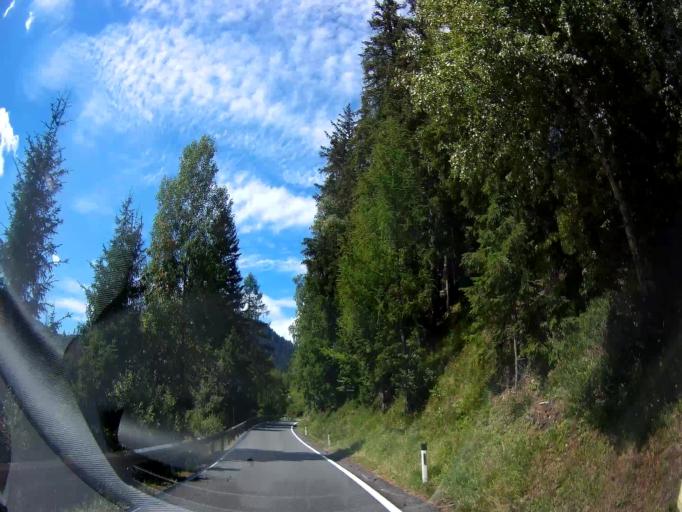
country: AT
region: Carinthia
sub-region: Politischer Bezirk Sankt Veit an der Glan
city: Glodnitz
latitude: 46.9211
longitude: 14.0564
